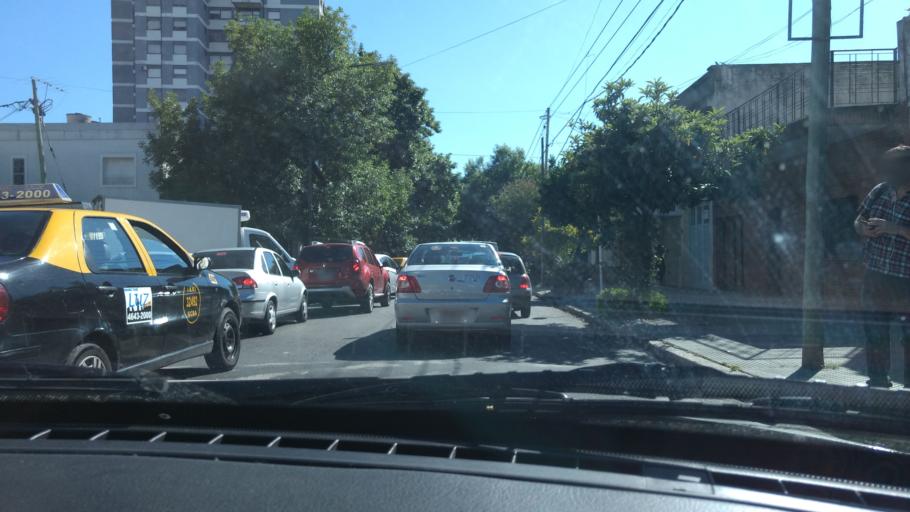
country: AR
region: Buenos Aires F.D.
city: Villa Santa Rita
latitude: -34.6242
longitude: -58.5241
